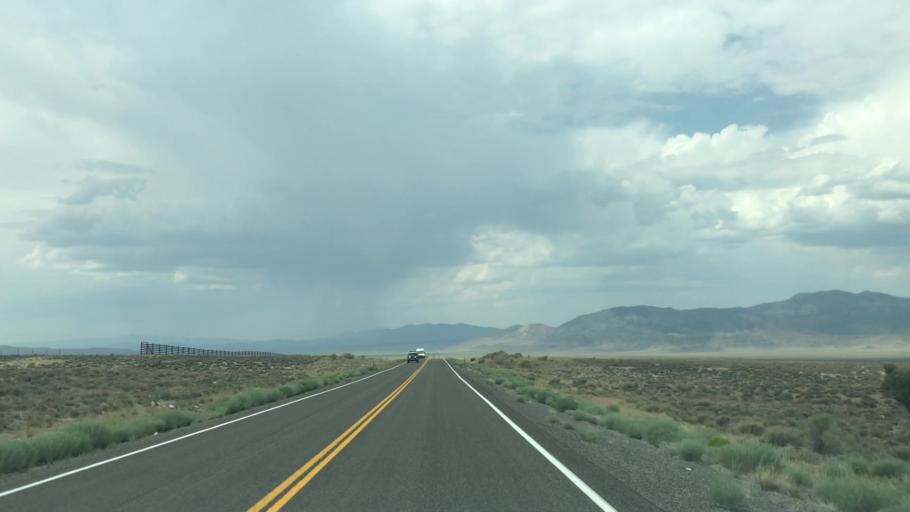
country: US
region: Nevada
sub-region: Eureka County
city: Eureka
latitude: 39.3923
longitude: -115.7310
